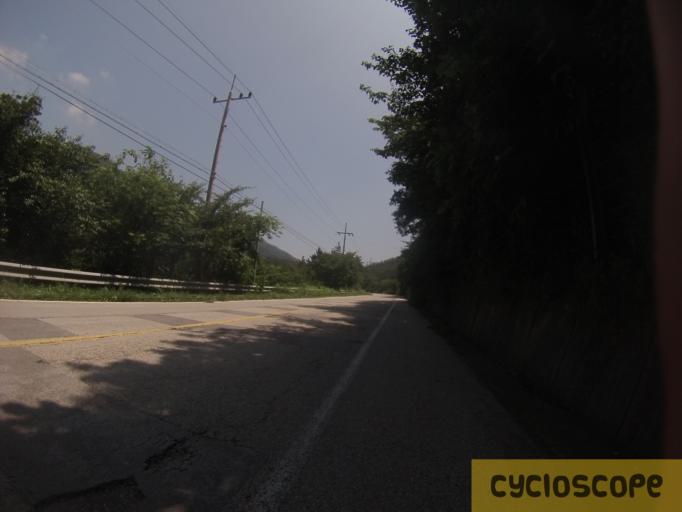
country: KR
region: Jeollabuk-do
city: Puan
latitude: 35.6242
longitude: 126.4726
